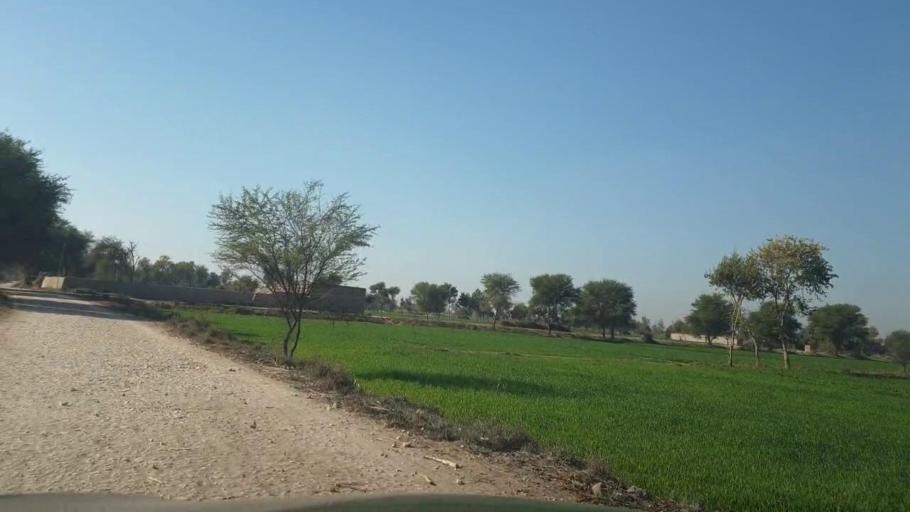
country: PK
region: Sindh
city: Mirpur Mathelo
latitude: 28.0041
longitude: 69.4795
